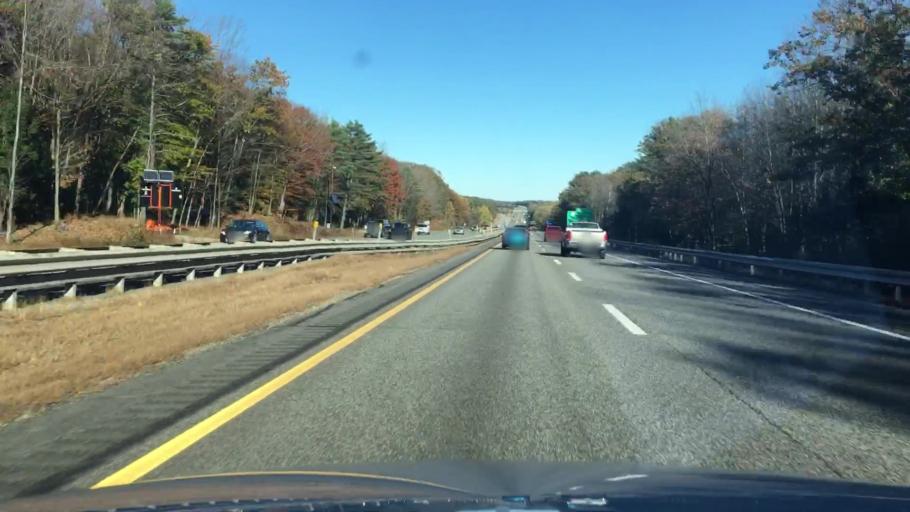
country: US
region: Maine
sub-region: Cumberland County
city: Freeport
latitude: 43.9067
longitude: -70.0542
